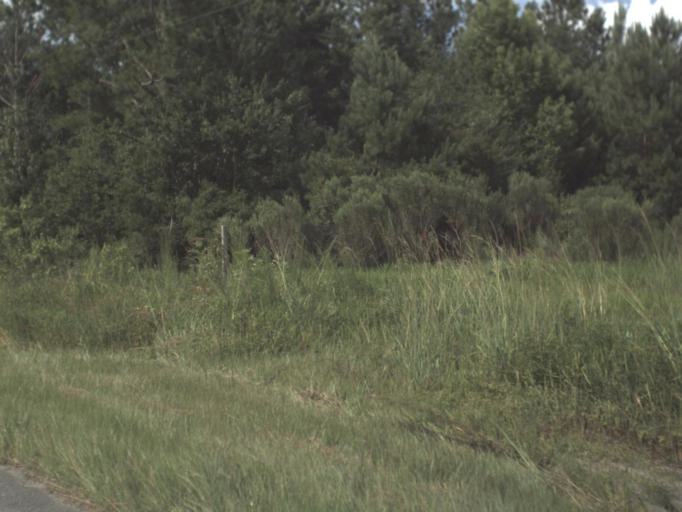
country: US
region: Florida
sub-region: Madison County
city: Madison
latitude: 30.3752
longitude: -83.6579
